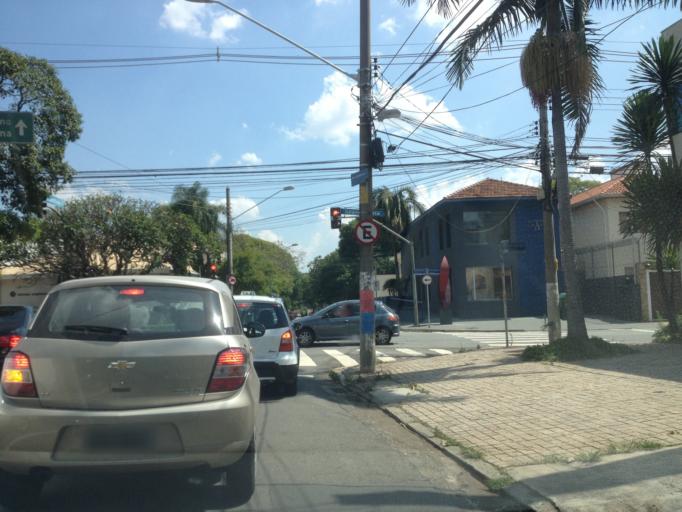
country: BR
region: Sao Paulo
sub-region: Sao Paulo
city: Sao Paulo
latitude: -23.5683
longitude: -46.6775
